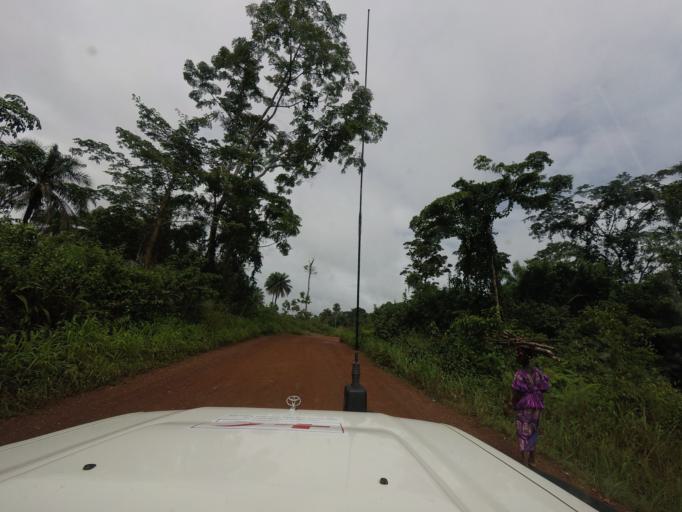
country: GN
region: Nzerekore
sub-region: Nzerekore Prefecture
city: Nzerekore
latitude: 7.7239
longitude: -8.8779
